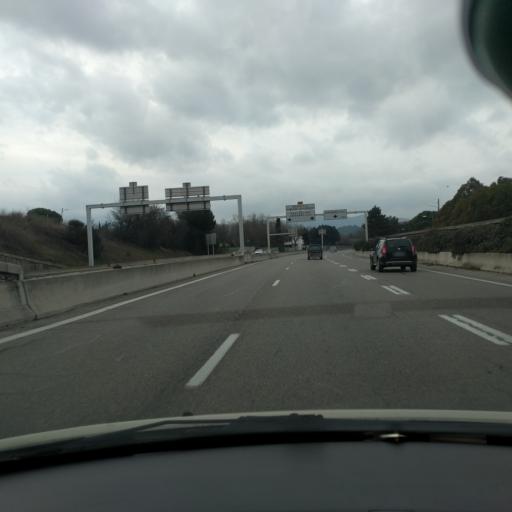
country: FR
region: Provence-Alpes-Cote d'Azur
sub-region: Departement des Bouches-du-Rhone
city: Gardanne
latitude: 43.4620
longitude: 5.4659
